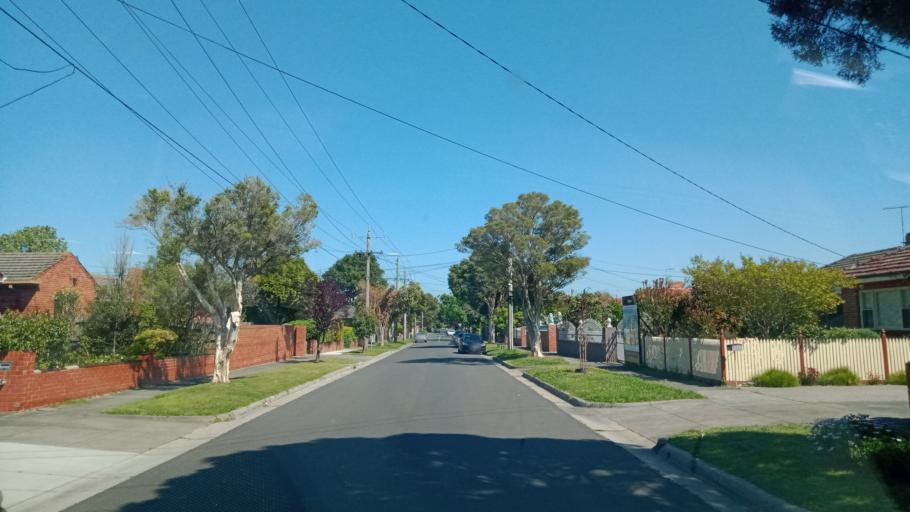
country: AU
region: Victoria
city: Murrumbeena
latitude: -37.9136
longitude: 145.0692
